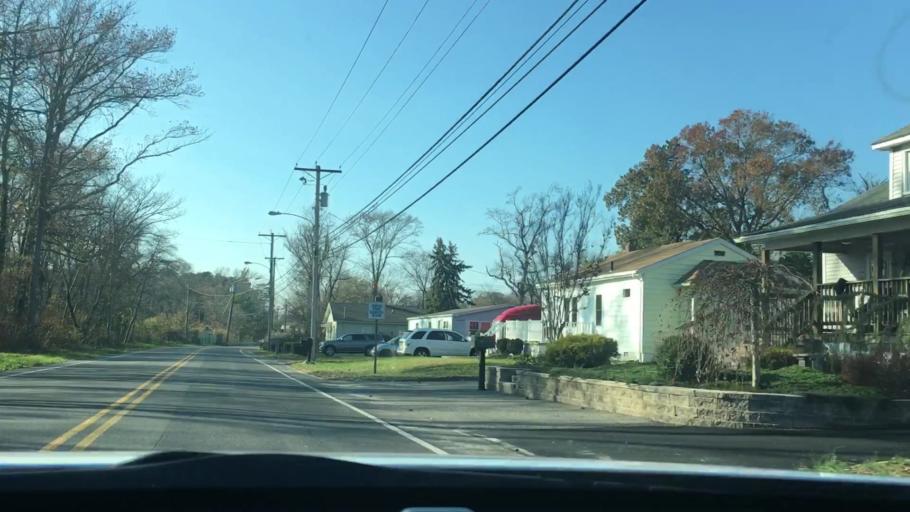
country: US
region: New Jersey
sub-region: Atlantic County
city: Absecon
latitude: 39.4137
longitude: -74.5049
